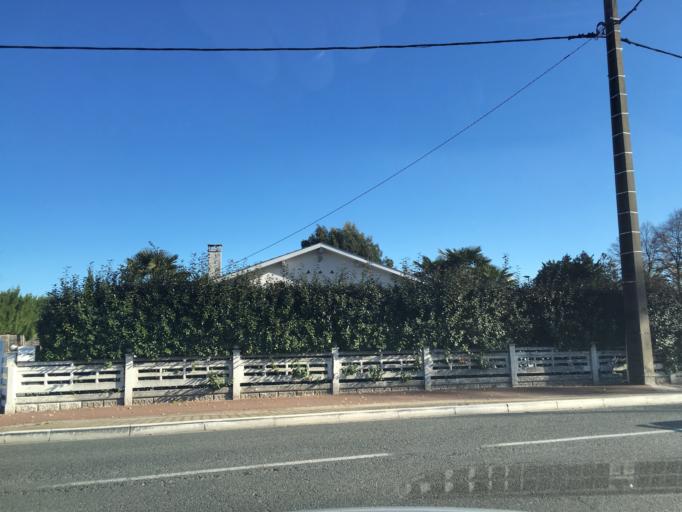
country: FR
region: Aquitaine
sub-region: Departement de la Gironde
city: La Teste-de-Buch
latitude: 44.6181
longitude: -1.1389
